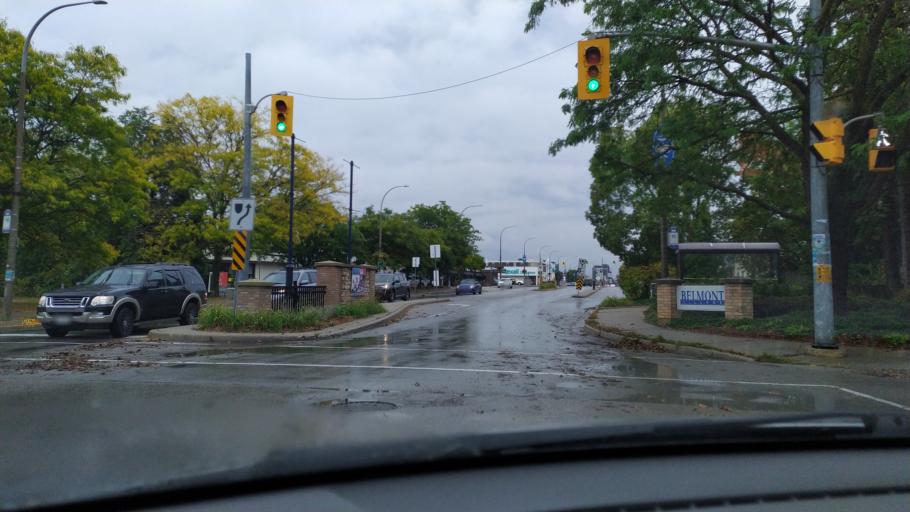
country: CA
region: Ontario
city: Waterloo
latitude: 43.4551
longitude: -80.5192
